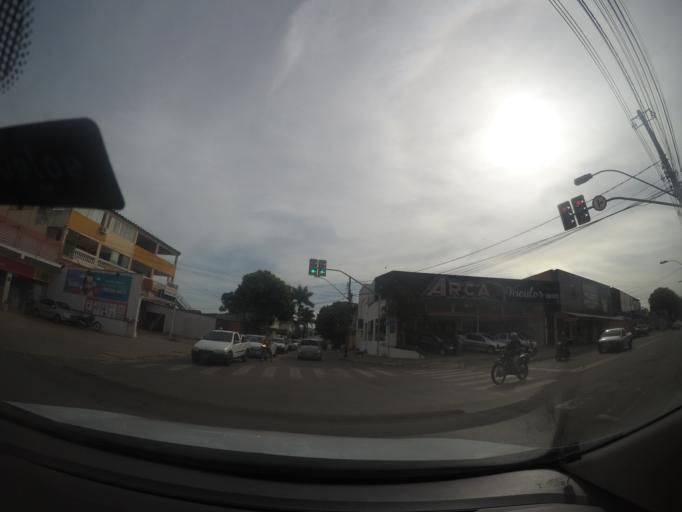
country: BR
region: Goias
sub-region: Goiania
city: Goiania
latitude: -16.6607
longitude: -49.3088
